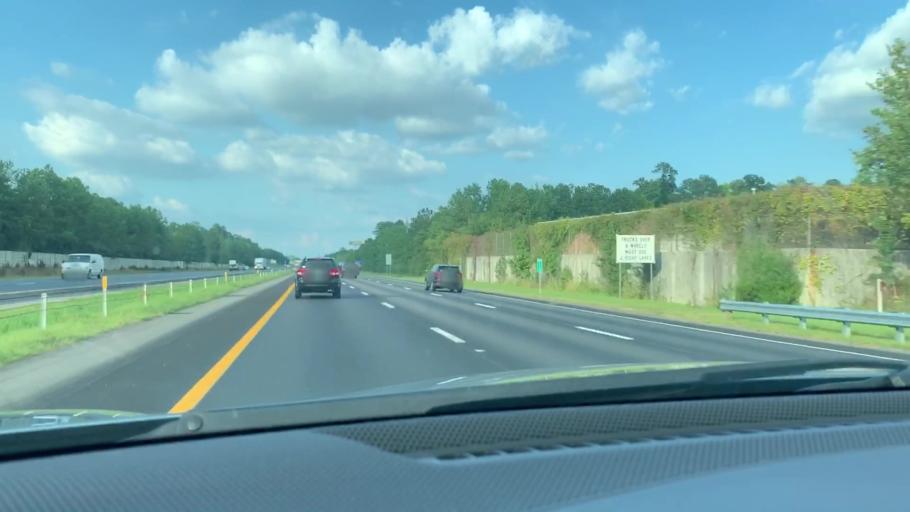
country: US
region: South Carolina
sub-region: Richland County
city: Forest Acres
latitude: 34.0041
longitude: -80.9572
